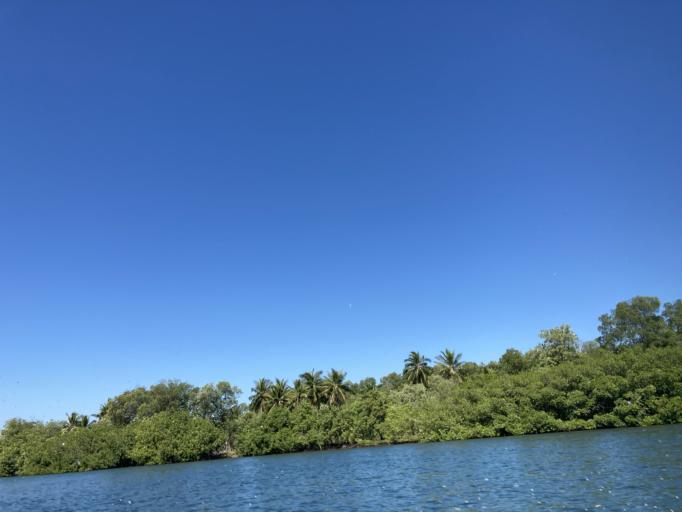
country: GT
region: Jutiapa
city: Pasaco
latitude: 13.8044
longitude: -90.2663
